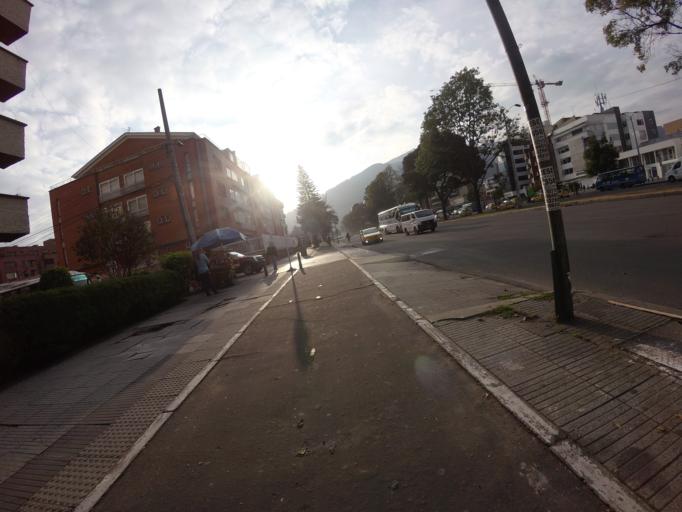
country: CO
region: Bogota D.C.
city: Barrio San Luis
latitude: 4.6841
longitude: -74.0457
